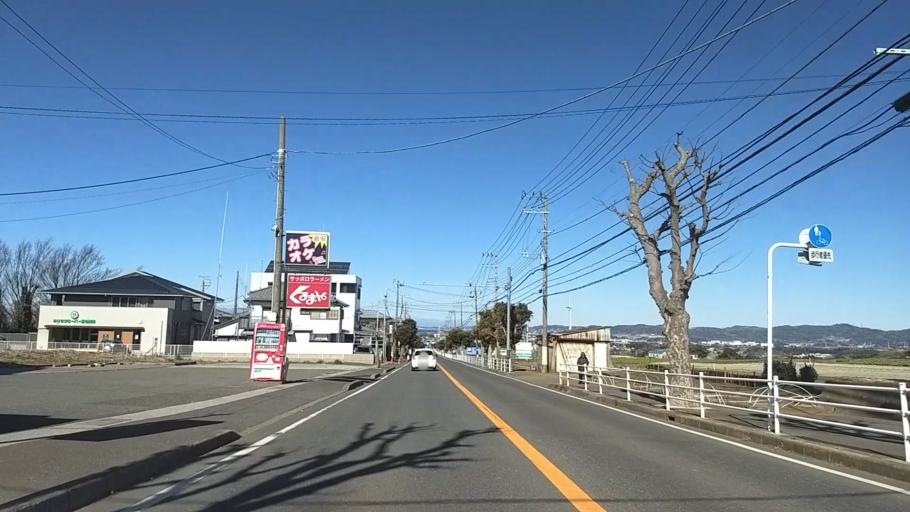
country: JP
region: Kanagawa
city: Miura
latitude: 35.1698
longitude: 139.6388
